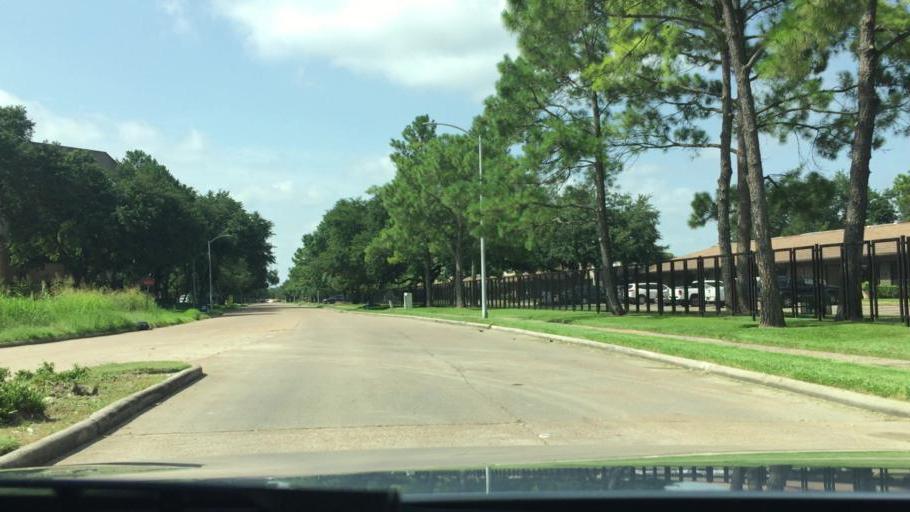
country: US
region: Texas
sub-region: Harris County
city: Hudson
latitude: 29.8502
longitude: -95.4949
